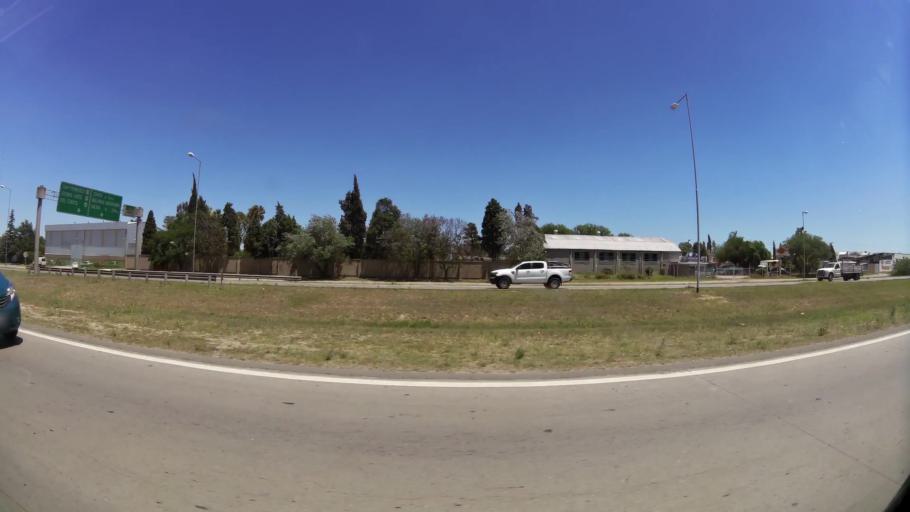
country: AR
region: Cordoba
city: Malvinas Argentinas
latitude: -31.3807
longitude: -64.1268
